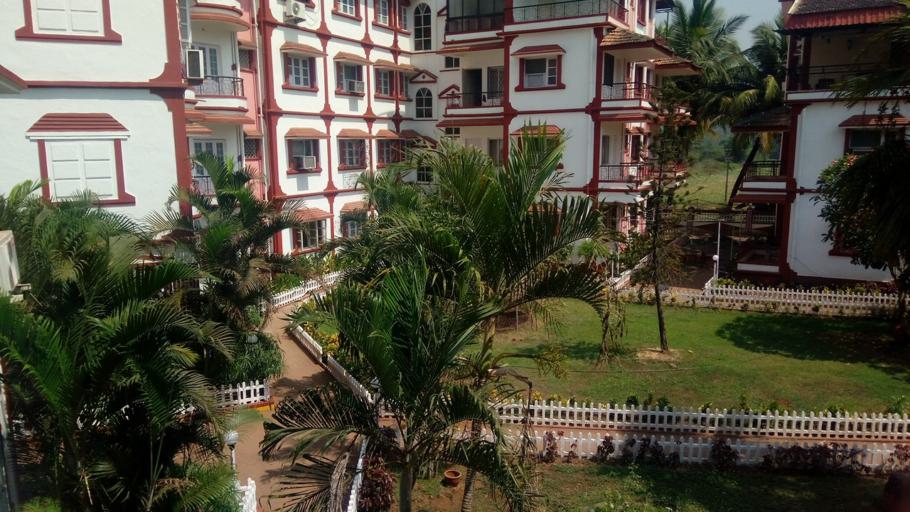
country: IN
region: Goa
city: Calangute
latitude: 15.5406
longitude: 73.7689
